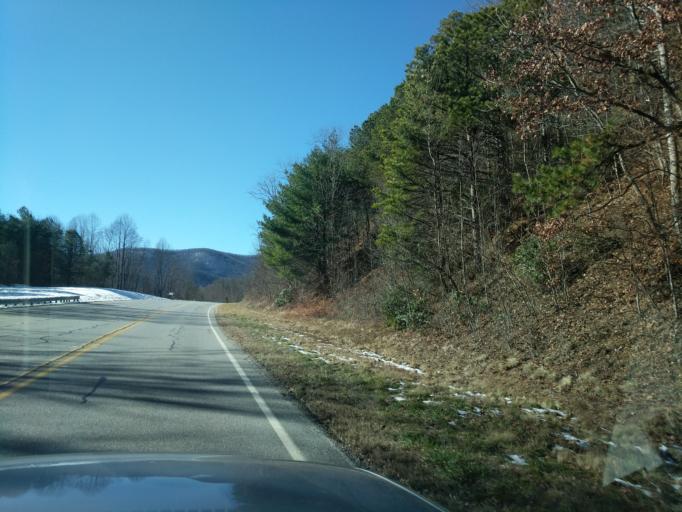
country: US
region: Georgia
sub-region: Towns County
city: Hiawassee
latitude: 34.8937
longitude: -83.5913
